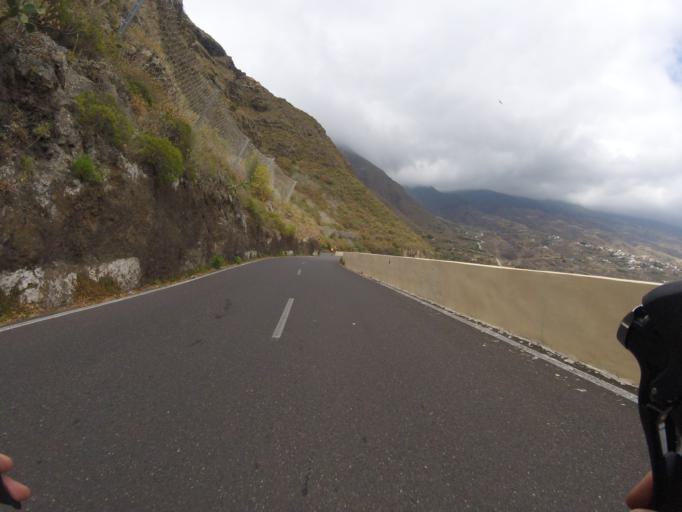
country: ES
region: Canary Islands
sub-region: Provincia de Santa Cruz de Tenerife
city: Guimar
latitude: 28.2953
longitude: -16.4111
